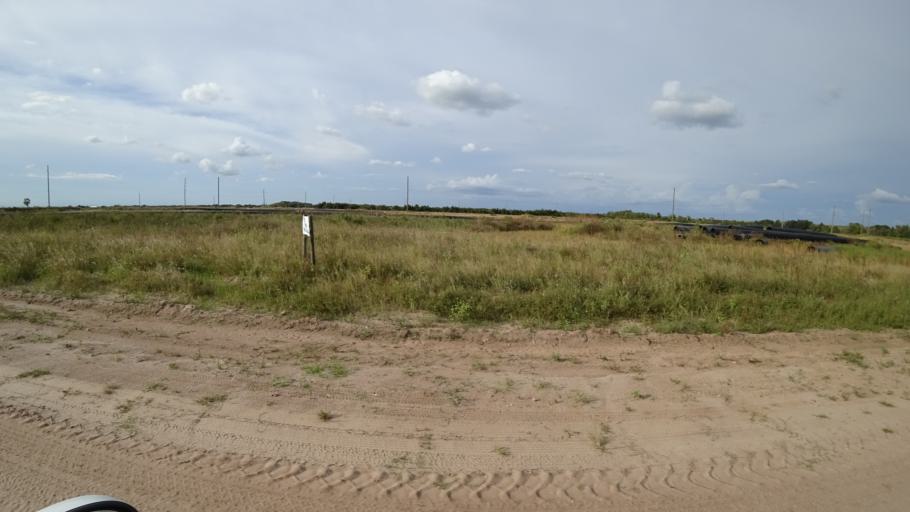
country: US
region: Florida
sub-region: Hardee County
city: Wauchula
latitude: 27.5279
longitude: -82.0739
